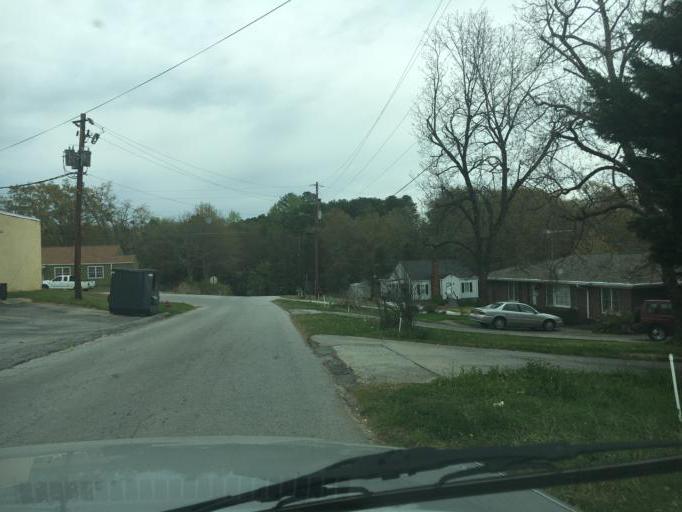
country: US
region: Georgia
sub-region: Stephens County
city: Toccoa
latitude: 34.5735
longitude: -83.3110
